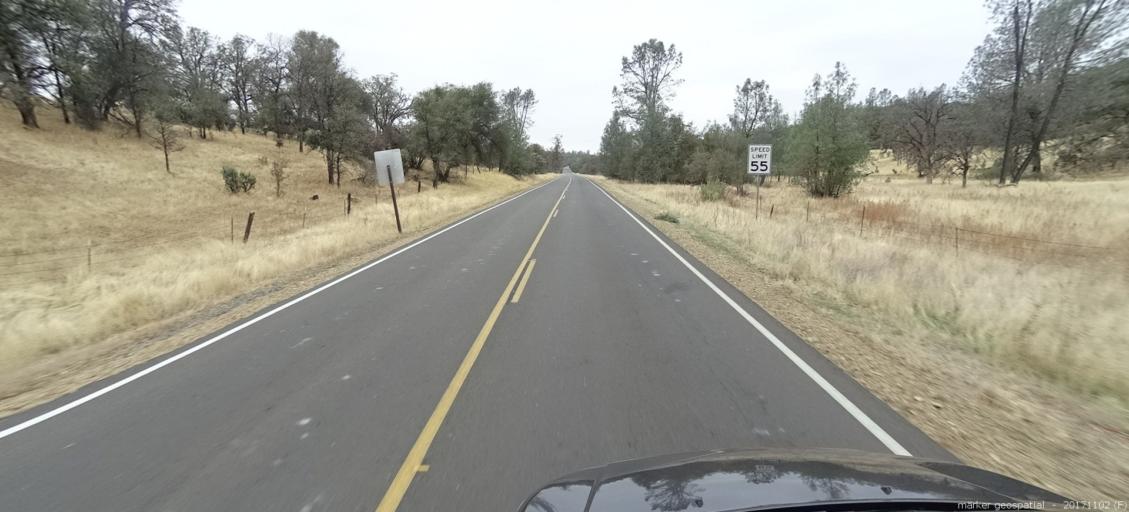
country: US
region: California
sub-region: Shasta County
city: Bella Vista
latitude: 40.7089
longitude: -122.2436
